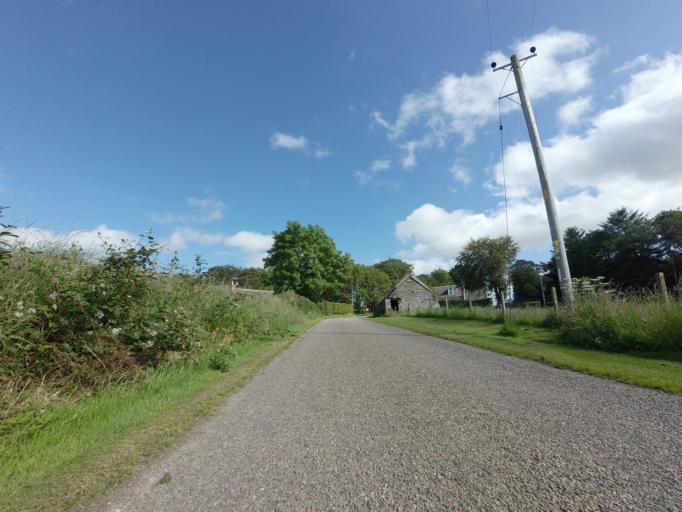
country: GB
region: Scotland
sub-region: Aberdeenshire
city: Turriff
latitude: 57.5934
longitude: -2.5083
